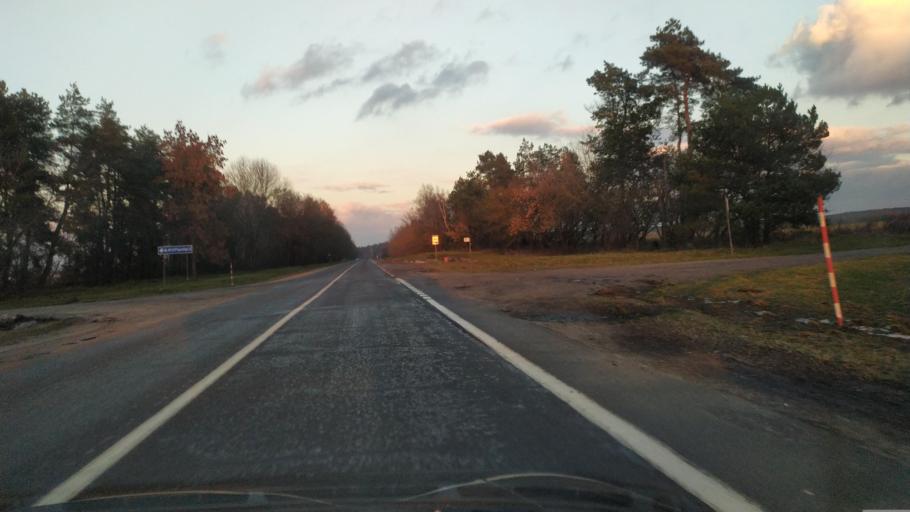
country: BY
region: Brest
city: Kamyanyets
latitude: 52.3819
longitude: 23.8096
